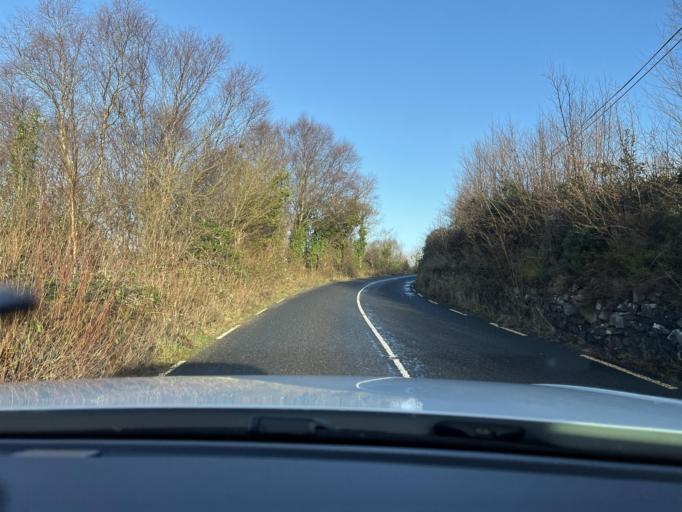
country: IE
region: Connaught
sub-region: County Leitrim
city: Manorhamilton
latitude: 54.2008
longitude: -7.9717
